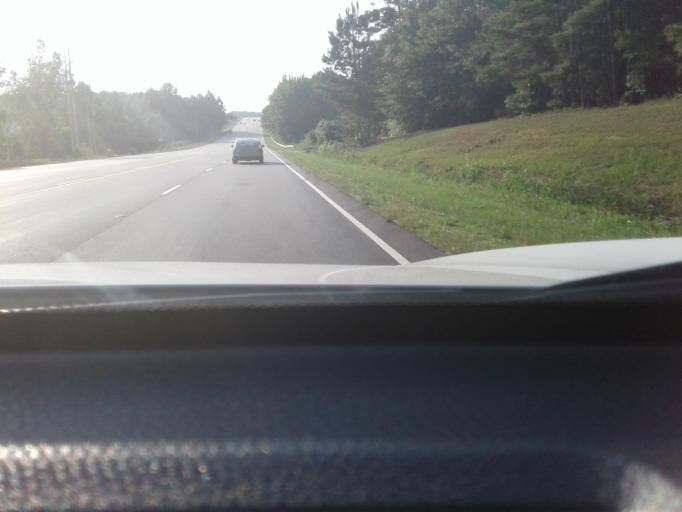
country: US
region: North Carolina
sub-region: Harnett County
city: Buies Creek
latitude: 35.3809
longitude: -78.7162
